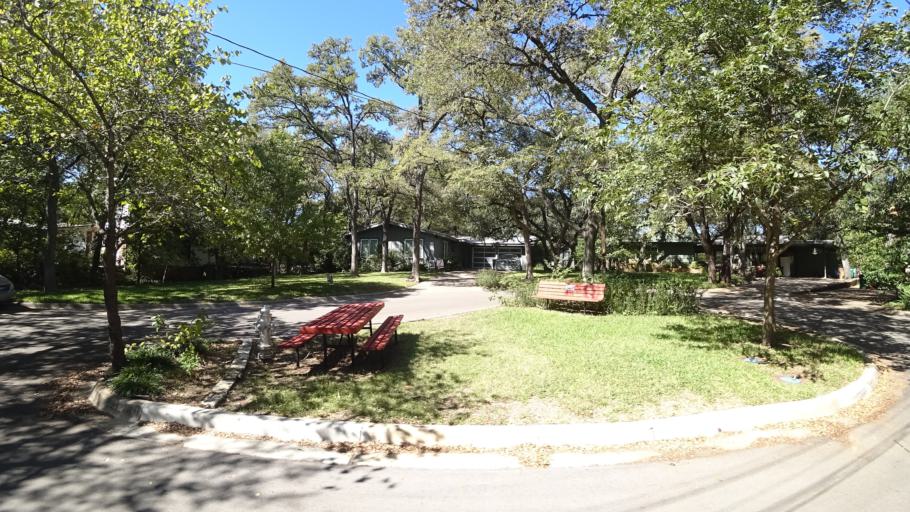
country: US
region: Texas
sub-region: Travis County
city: Austin
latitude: 30.3291
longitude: -97.7475
